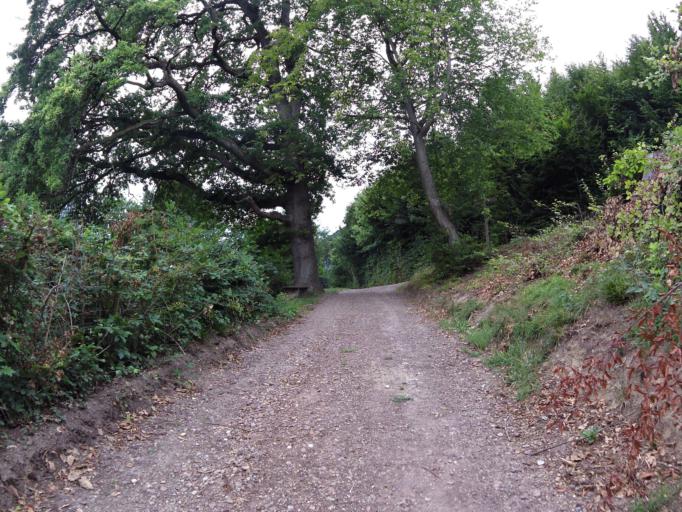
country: DE
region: Baden-Wuerttemberg
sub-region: Freiburg Region
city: Hohberg
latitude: 48.3417
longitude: 7.9043
